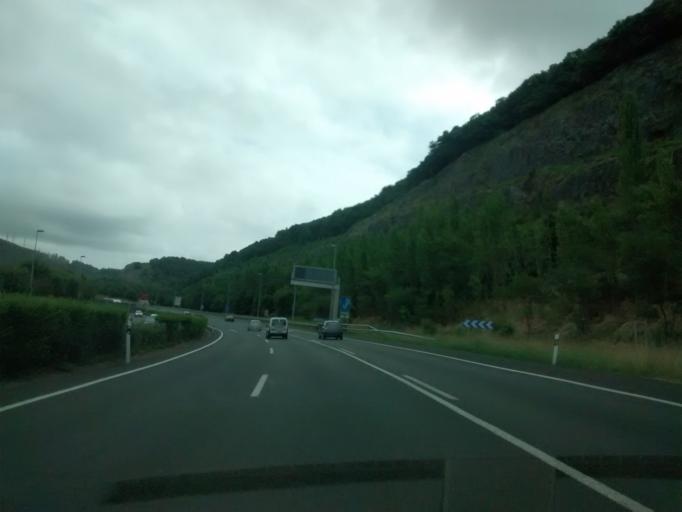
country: ES
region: Cantabria
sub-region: Provincia de Cantabria
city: Hazas de Cesto
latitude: 43.4016
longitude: -3.6292
